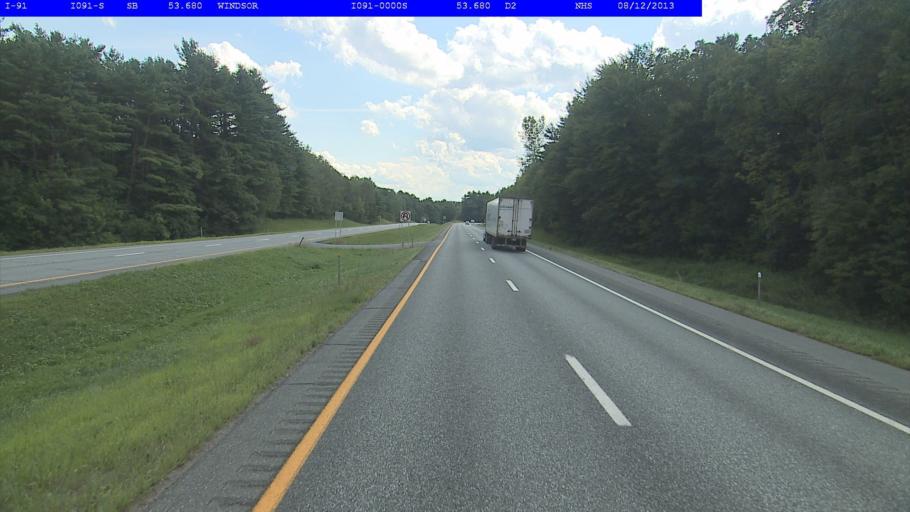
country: US
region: Vermont
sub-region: Windsor County
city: Windsor
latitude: 43.4333
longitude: -72.4029
